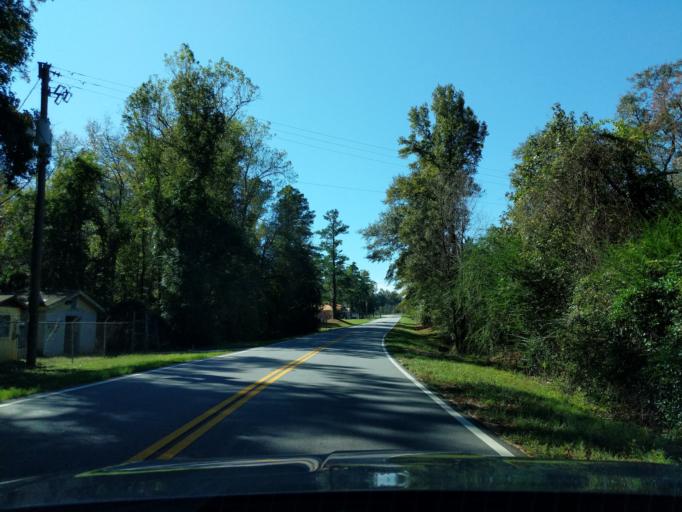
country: US
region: Georgia
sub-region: Richmond County
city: Hephzibah
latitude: 33.3014
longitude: -82.0195
